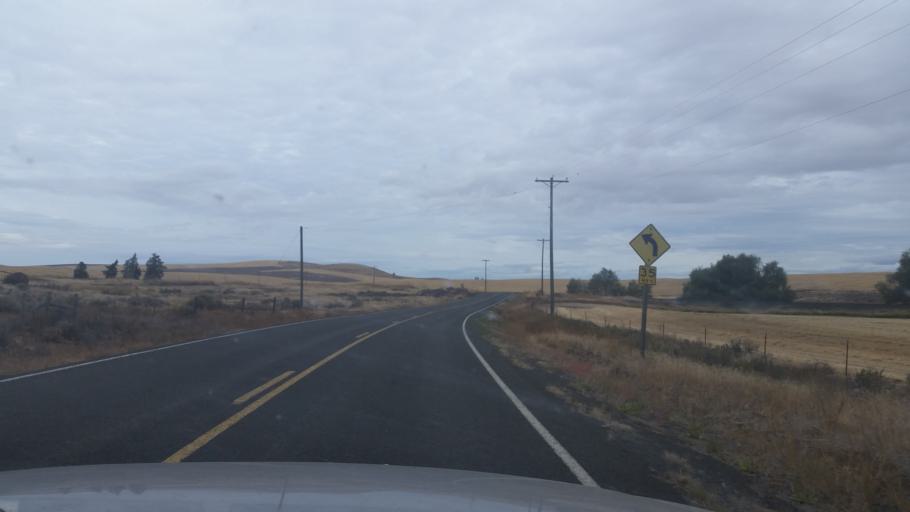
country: US
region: Washington
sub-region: Spokane County
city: Medical Lake
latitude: 47.5196
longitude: -117.9004
